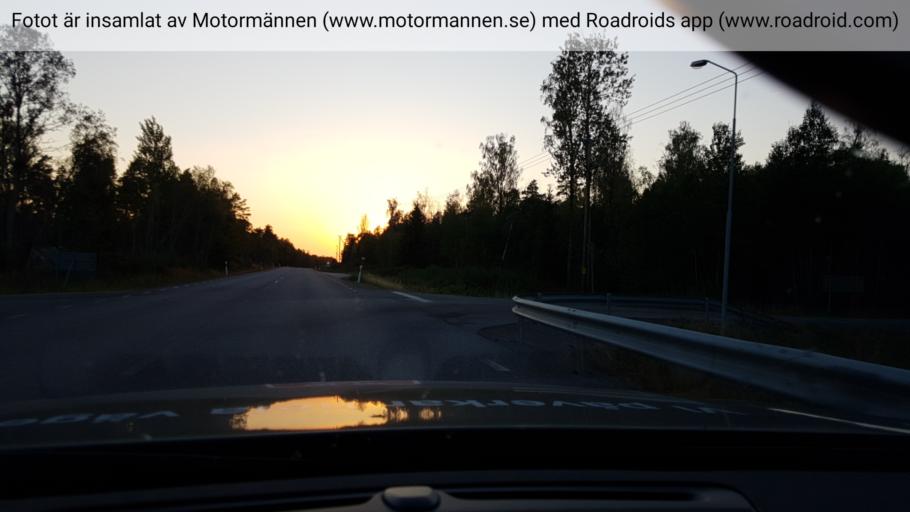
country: SE
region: Uppsala
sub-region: Osthammars Kommun
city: Bjorklinge
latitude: 59.9696
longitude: 17.3723
